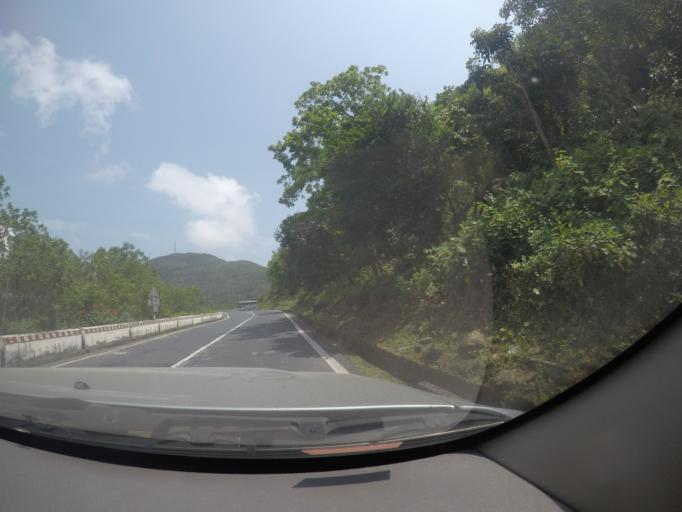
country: VN
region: Da Nang
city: Lien Chieu
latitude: 16.1932
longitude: 108.1235
